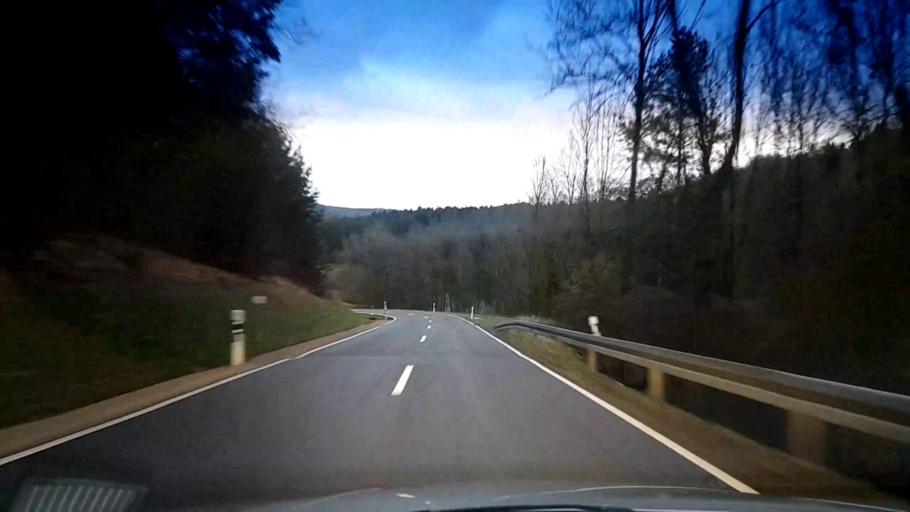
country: DE
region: Bavaria
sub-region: Upper Franconia
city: Schesslitz
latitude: 50.0193
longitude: 11.0650
